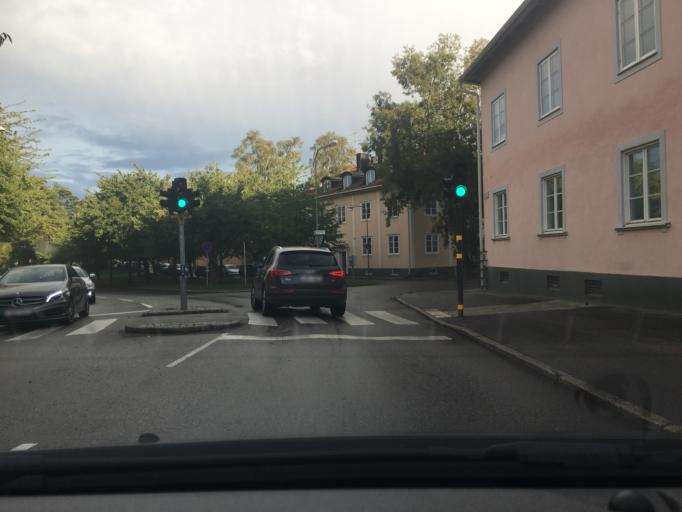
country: SE
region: Stockholm
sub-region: Stockholms Kommun
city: Bromma
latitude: 59.3287
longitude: 17.9690
